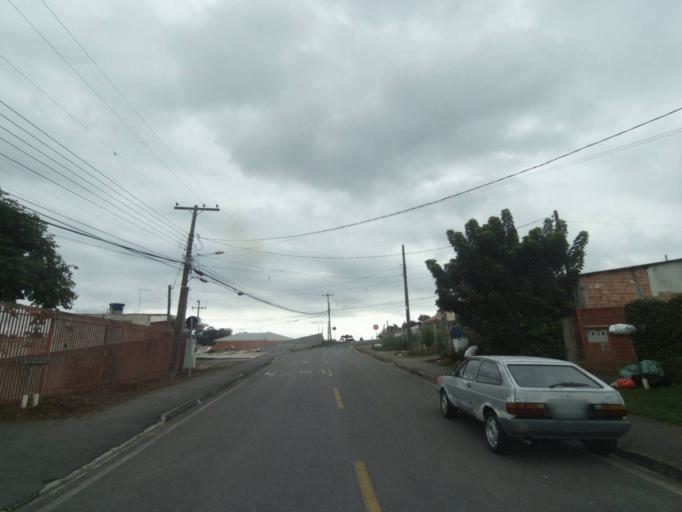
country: BR
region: Parana
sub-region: Quatro Barras
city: Quatro Barras
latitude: -25.3526
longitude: -49.1124
